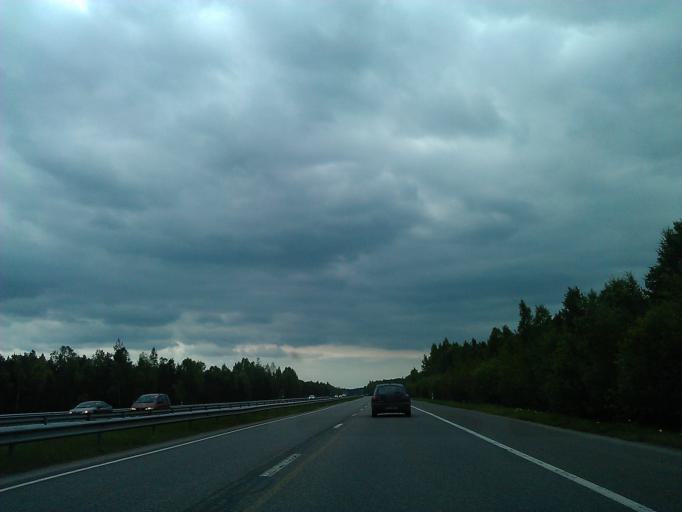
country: LV
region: Marupe
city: Marupe
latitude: 56.8680
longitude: 24.0663
